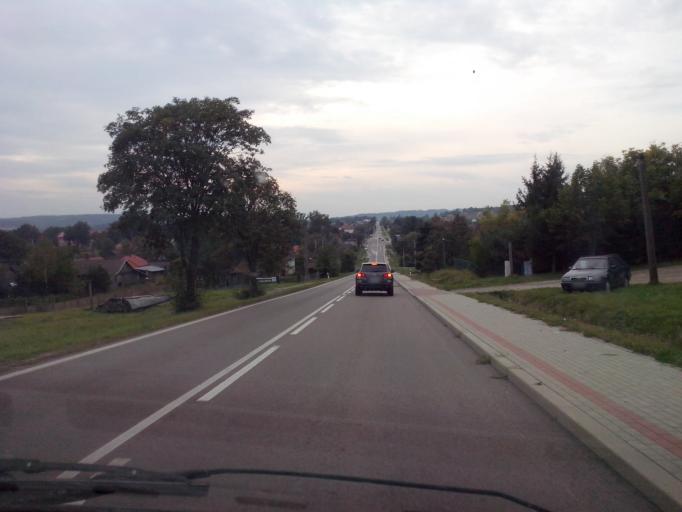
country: PL
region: Subcarpathian Voivodeship
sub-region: Powiat przemyski
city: Nienadowa
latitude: 49.8193
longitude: 22.4275
